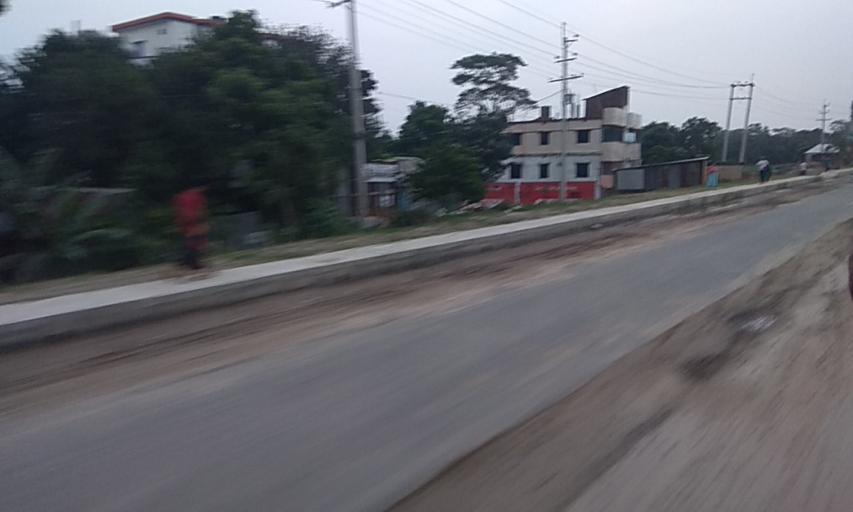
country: BD
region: Dhaka
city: Char Bhadrasan
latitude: 23.3734
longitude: 90.0285
